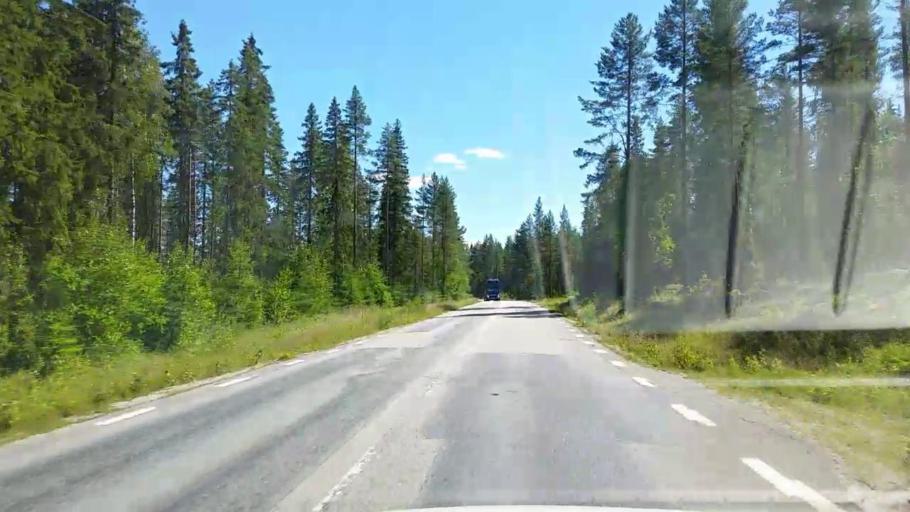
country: SE
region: Gaevleborg
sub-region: Ovanakers Kommun
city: Edsbyn
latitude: 61.3421
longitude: 15.8211
